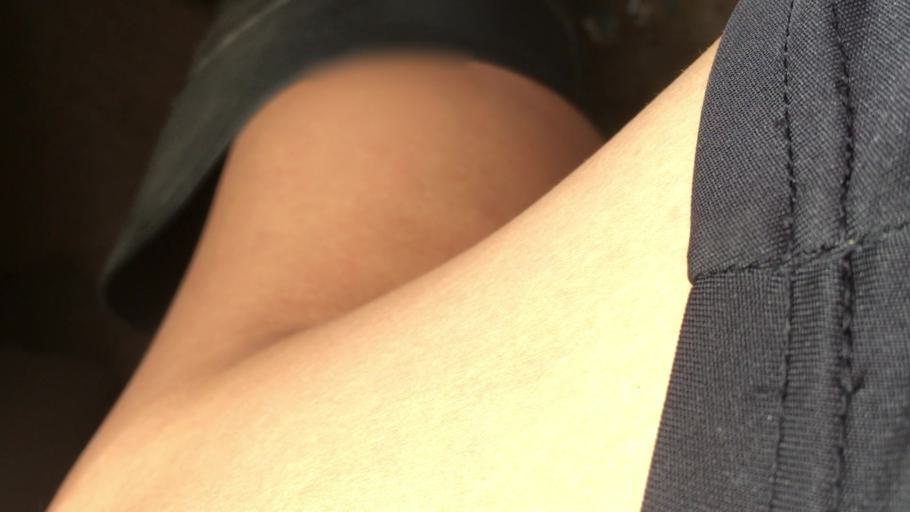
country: US
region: Maryland
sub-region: Worcester County
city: Pocomoke City
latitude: 38.0653
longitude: -75.5058
